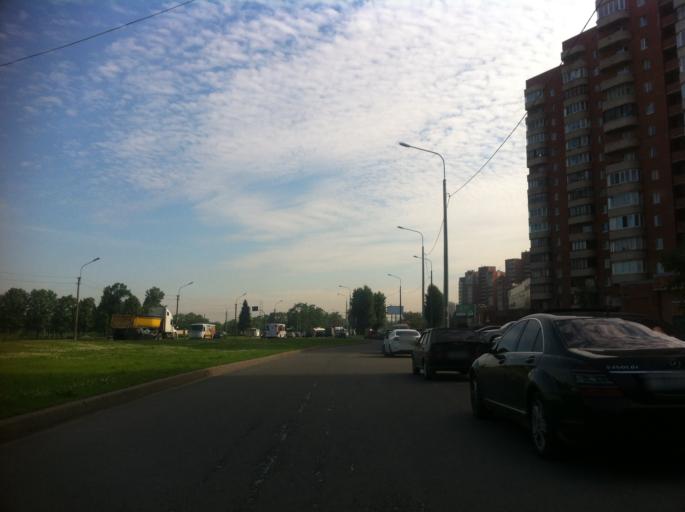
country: RU
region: St.-Petersburg
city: Uritsk
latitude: 59.8308
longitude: 30.1924
